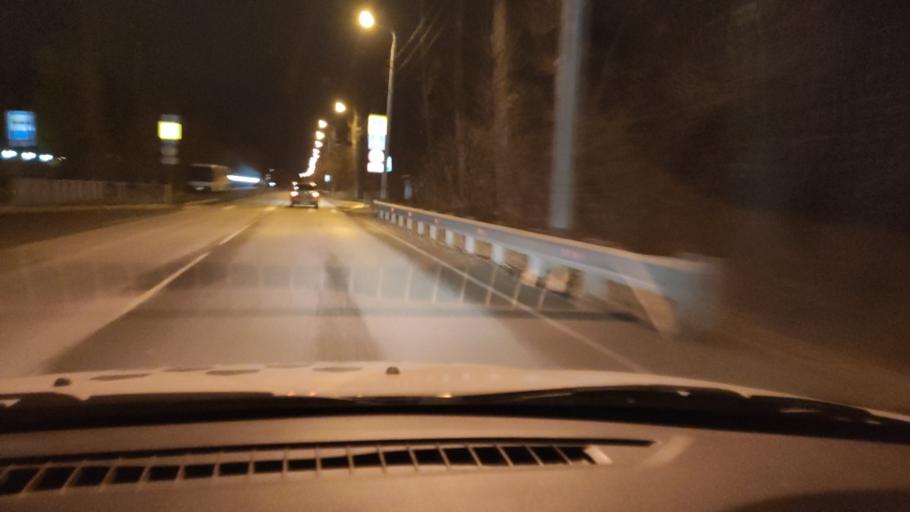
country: RU
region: Perm
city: Kondratovo
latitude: 57.9717
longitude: 56.1279
